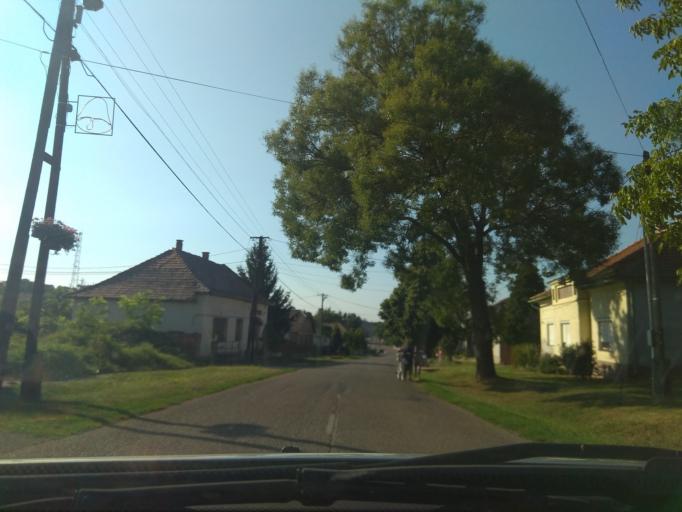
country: HU
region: Borsod-Abauj-Zemplen
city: Emod
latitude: 47.9442
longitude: 20.8136
